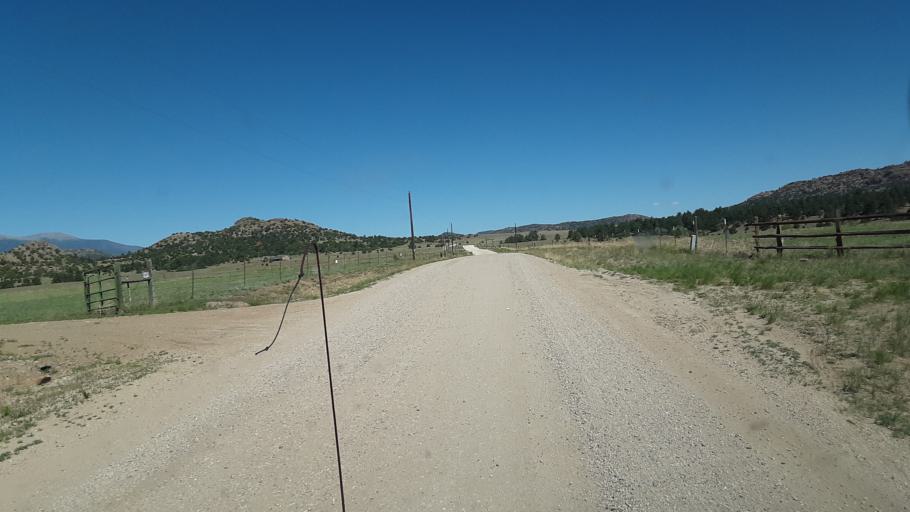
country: US
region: Colorado
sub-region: Custer County
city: Westcliffe
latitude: 38.2153
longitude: -105.4472
